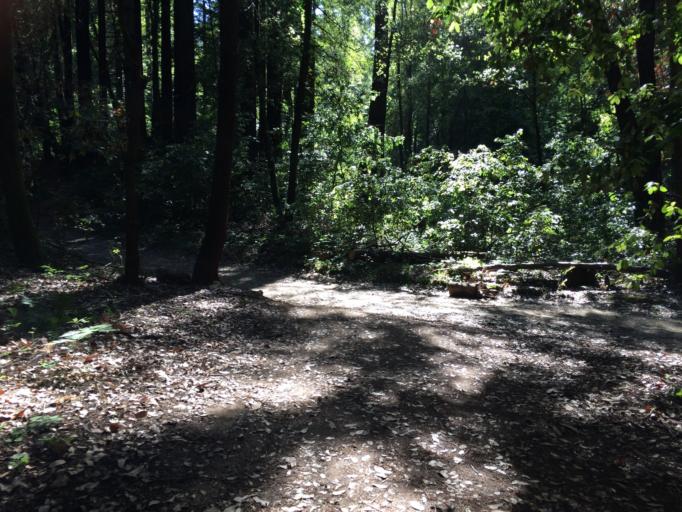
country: US
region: California
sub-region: Santa Cruz County
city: Mount Hermon
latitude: 37.0322
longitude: -122.0618
